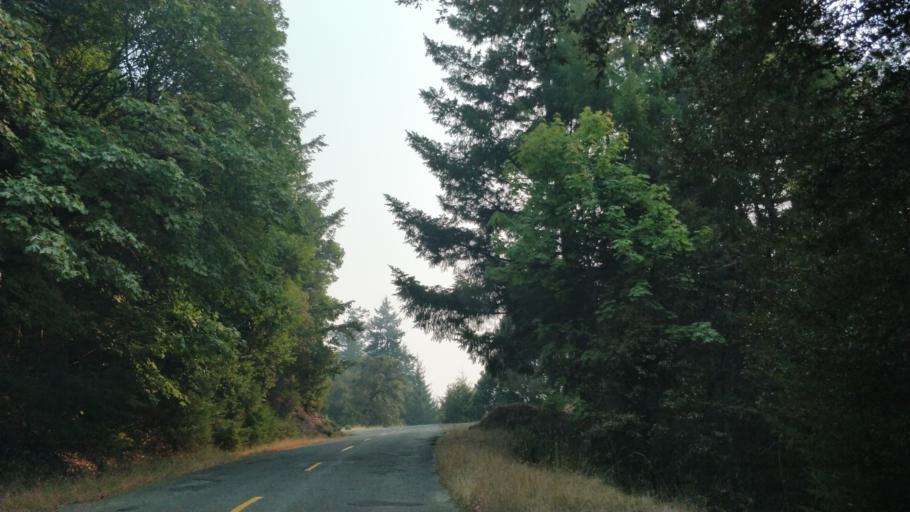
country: US
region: California
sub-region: Humboldt County
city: Rio Dell
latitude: 40.2559
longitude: -124.1193
